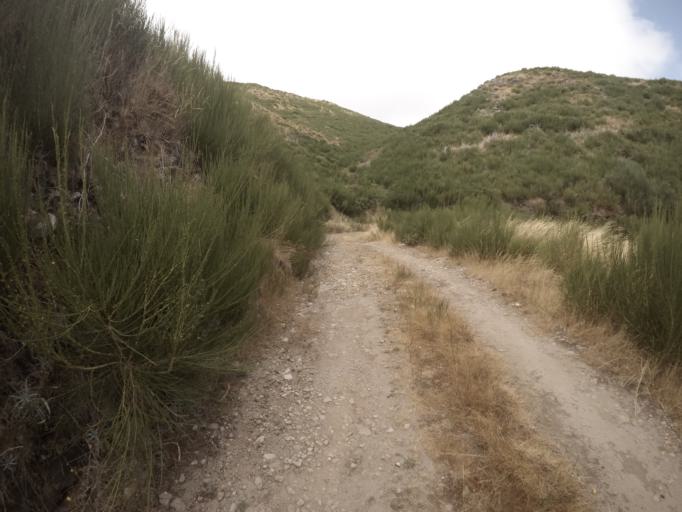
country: PT
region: Madeira
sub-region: Camara de Lobos
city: Curral das Freiras
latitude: 32.7106
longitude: -16.9909
